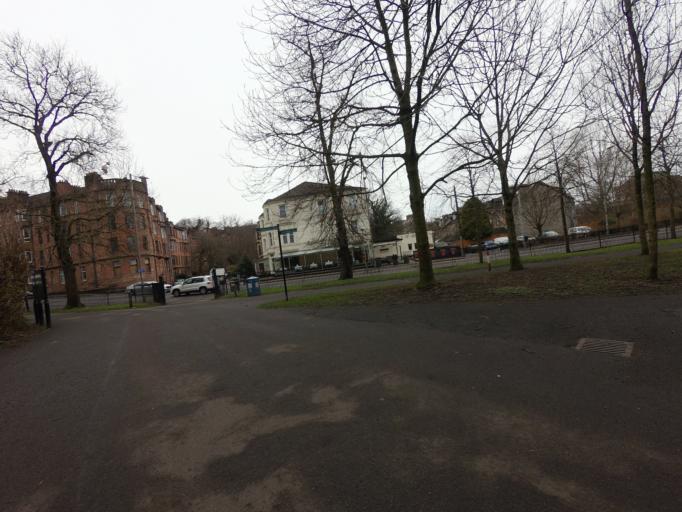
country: GB
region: Scotland
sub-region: East Renfrewshire
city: Giffnock
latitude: 55.8289
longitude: -4.2733
